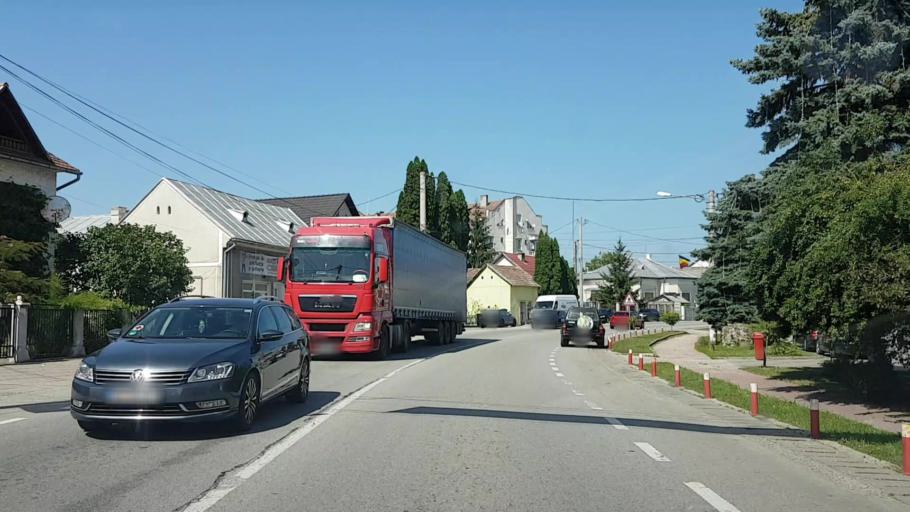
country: RO
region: Bistrita-Nasaud
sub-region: Comuna Beclean
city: Beclean
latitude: 47.1817
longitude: 24.1820
